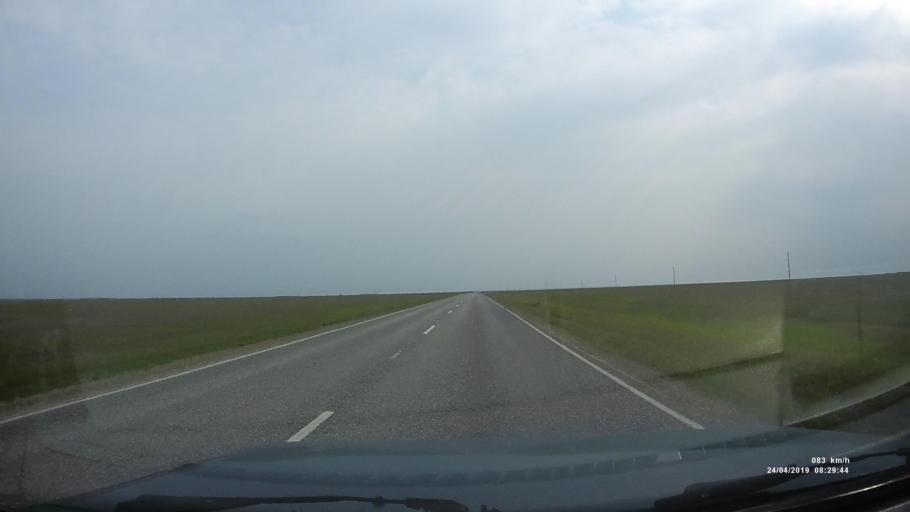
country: RU
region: Kalmykiya
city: Priyutnoye
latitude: 46.1544
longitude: 43.8353
